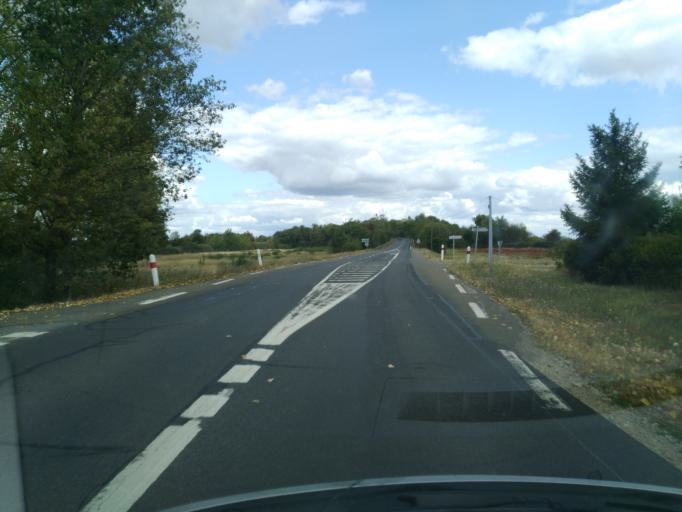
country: FR
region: Ile-de-France
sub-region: Departement des Yvelines
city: Ablis
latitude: 48.5340
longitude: 1.8697
